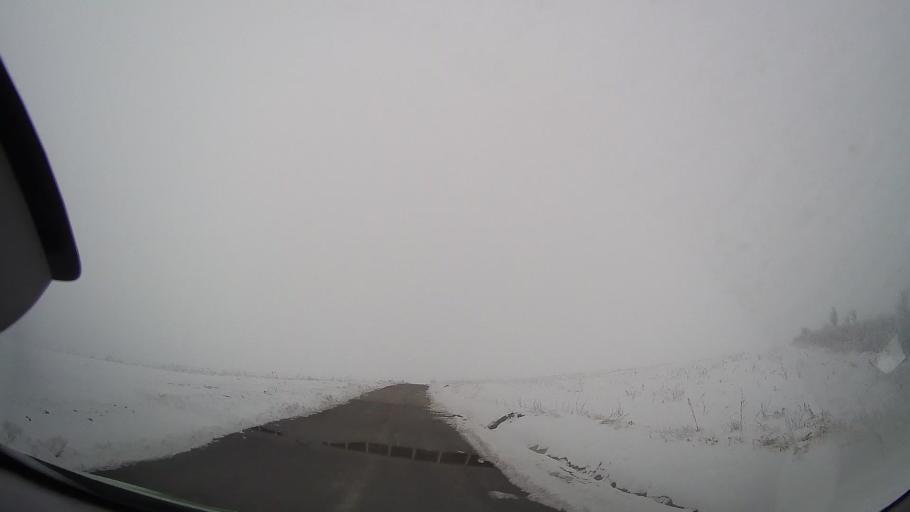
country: RO
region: Iasi
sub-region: Comuna Dagata
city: Dagata
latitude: 46.9074
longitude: 27.1969
